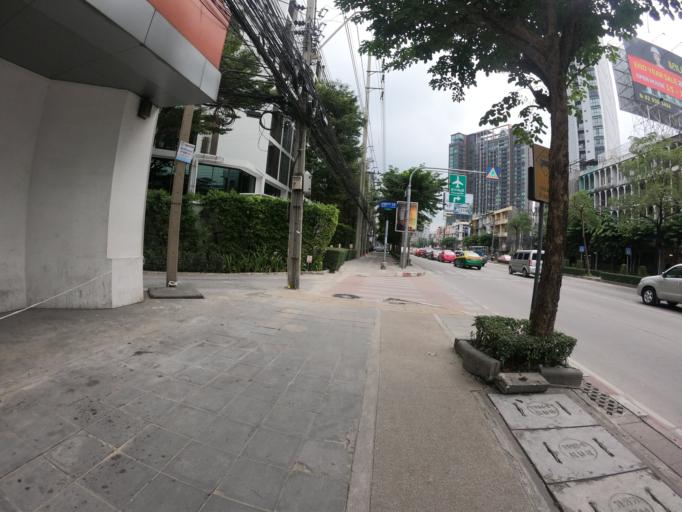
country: TH
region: Bangkok
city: Chatuchak
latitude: 13.8070
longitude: 100.5723
